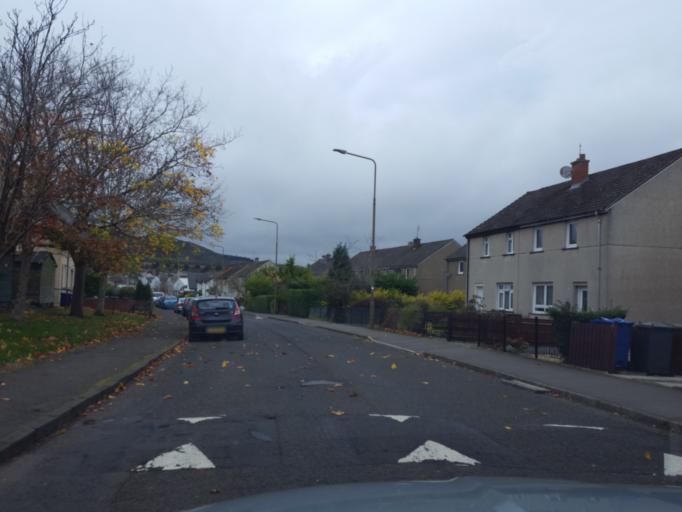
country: GB
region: Scotland
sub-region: Midlothian
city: Penicuik
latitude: 55.8311
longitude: -3.2129
